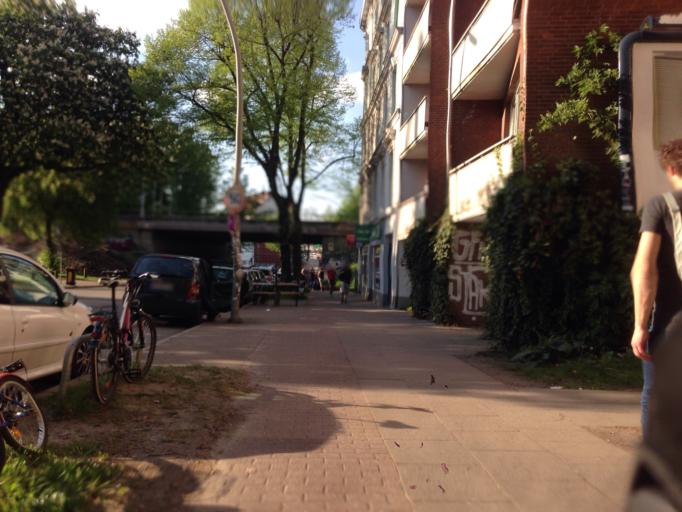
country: DE
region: Hamburg
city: Altona
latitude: 53.5588
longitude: 9.9279
